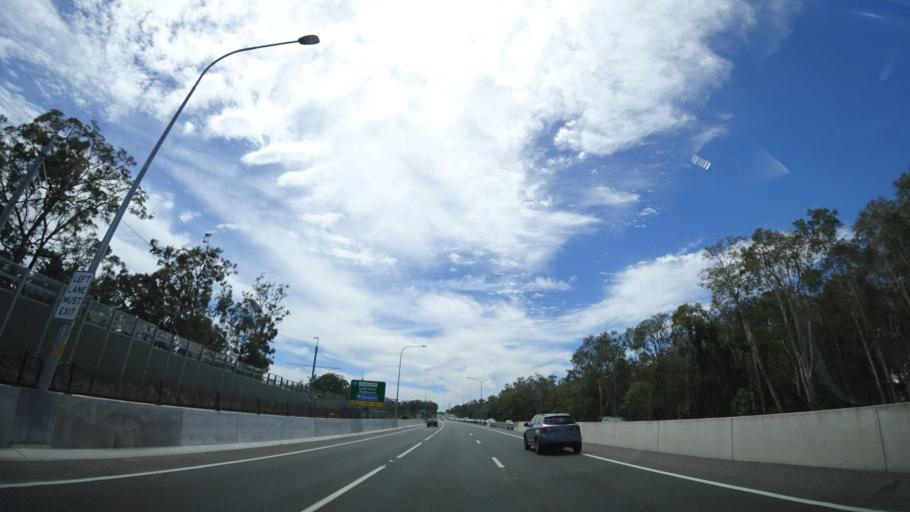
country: AU
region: Queensland
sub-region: Gold Coast
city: Southport
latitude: -27.9640
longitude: 153.3700
